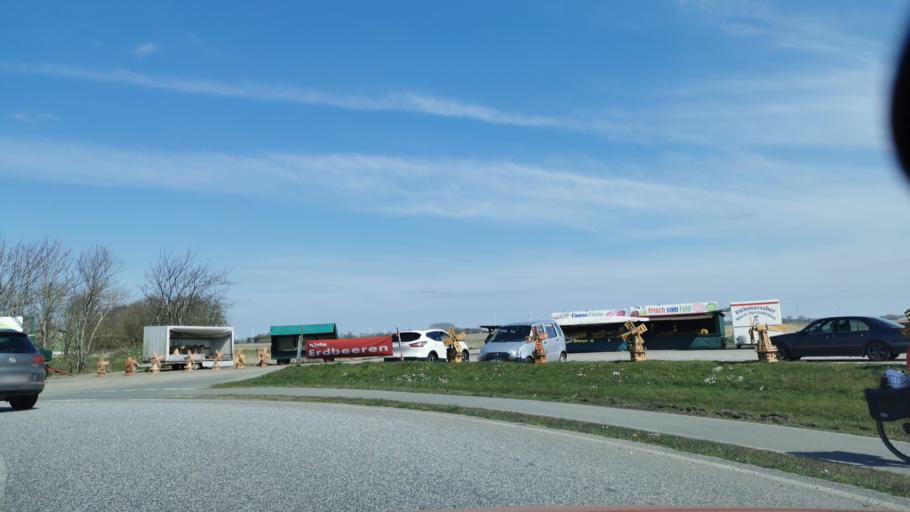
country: DE
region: Schleswig-Holstein
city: Oesterdeichstrich
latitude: 54.1462
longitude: 8.8773
